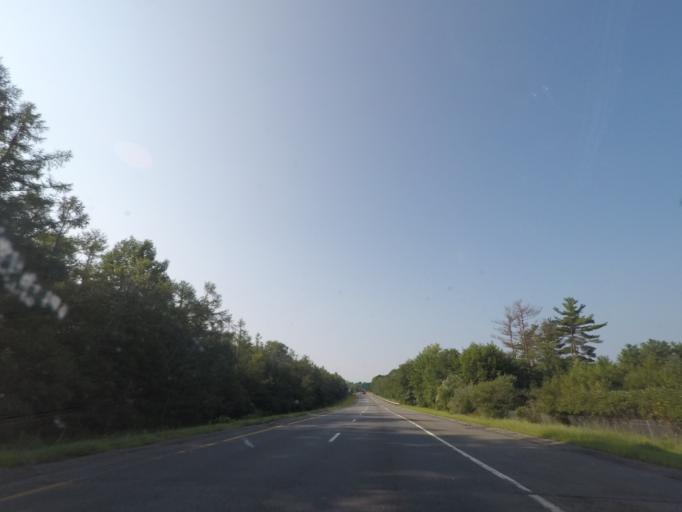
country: US
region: Massachusetts
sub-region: Worcester County
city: Oxford
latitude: 42.0875
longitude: -71.8663
